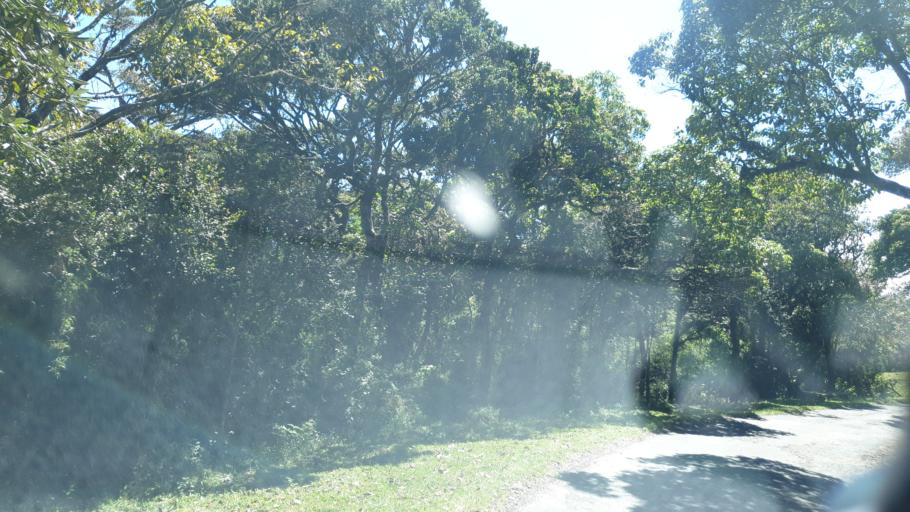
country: LK
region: Uva
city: Haputale
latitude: 6.8016
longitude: 80.8342
